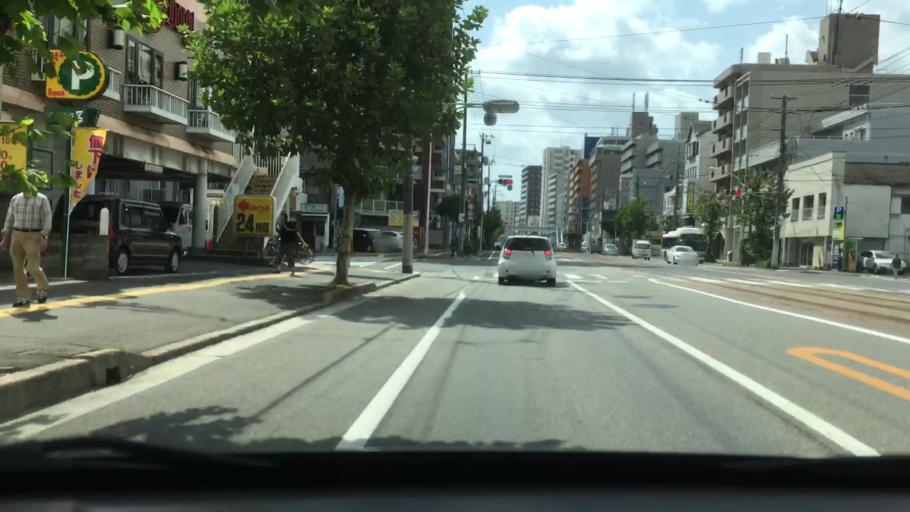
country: JP
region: Hiroshima
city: Hiroshima-shi
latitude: 34.3819
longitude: 132.4404
